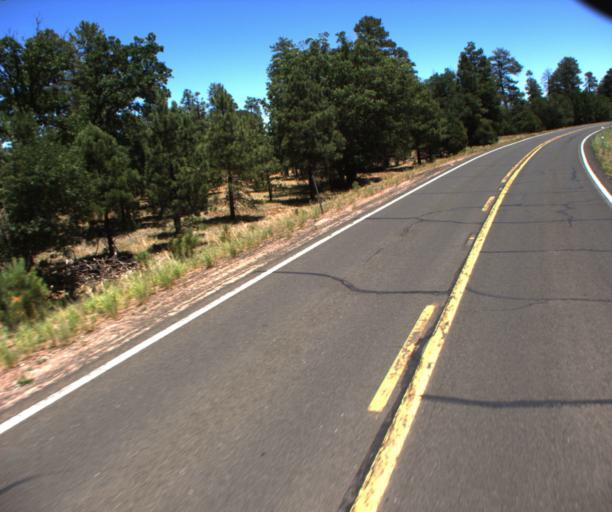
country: US
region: Arizona
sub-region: Gila County
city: Pine
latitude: 34.6230
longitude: -111.1637
